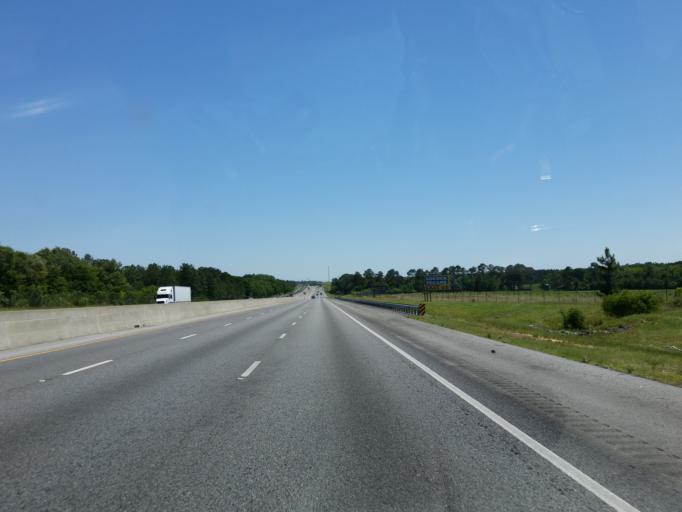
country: US
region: Georgia
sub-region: Turner County
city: Ashburn
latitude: 31.6074
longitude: -83.5647
